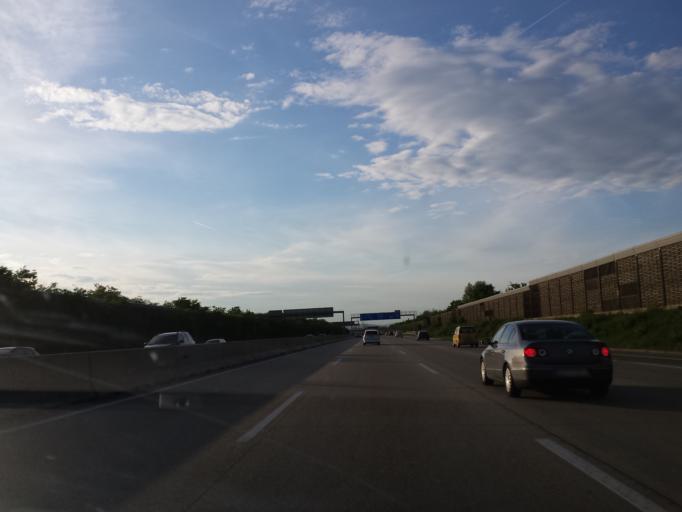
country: AT
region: Lower Austria
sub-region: Politischer Bezirk Modling
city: Biedermannsdorf
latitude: 48.0857
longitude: 16.3314
